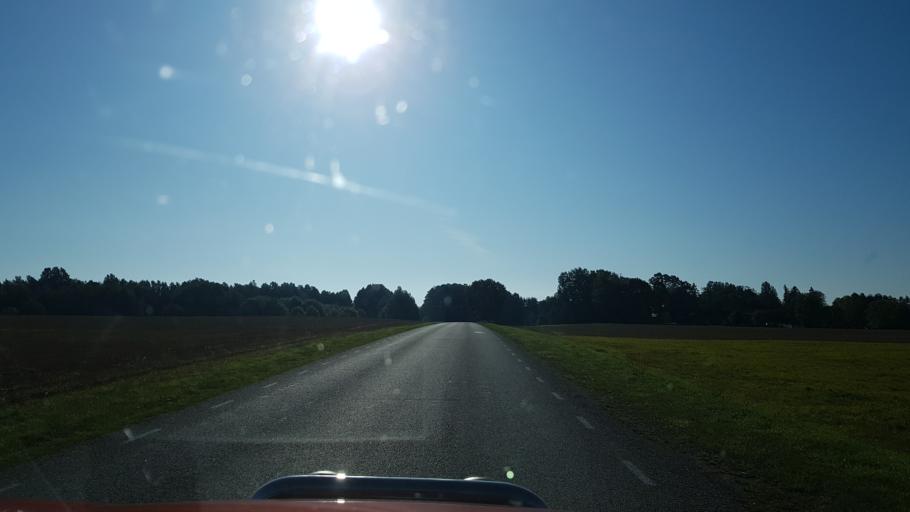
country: EE
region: Jogevamaa
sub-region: Tabivere vald
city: Tabivere
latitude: 58.6813
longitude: 26.6176
